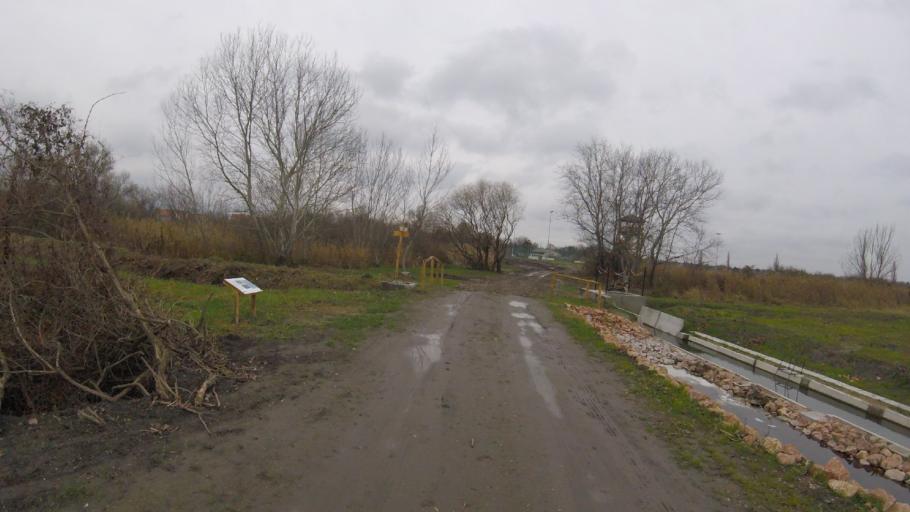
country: HU
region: Komarom-Esztergom
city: Tata
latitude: 47.6540
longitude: 18.3074
